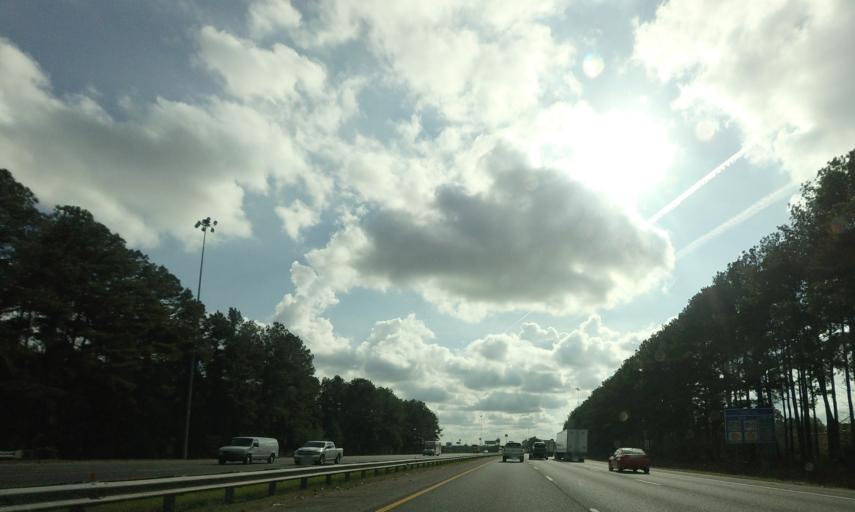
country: US
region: Georgia
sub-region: Houston County
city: Perry
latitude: 32.4792
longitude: -83.7424
